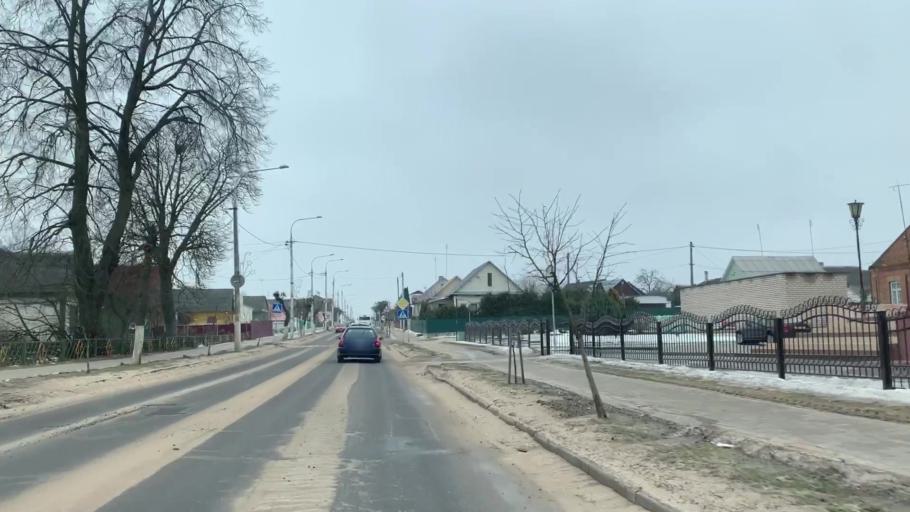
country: BY
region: Minsk
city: Nyasvizh
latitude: 53.2246
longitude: 26.6717
